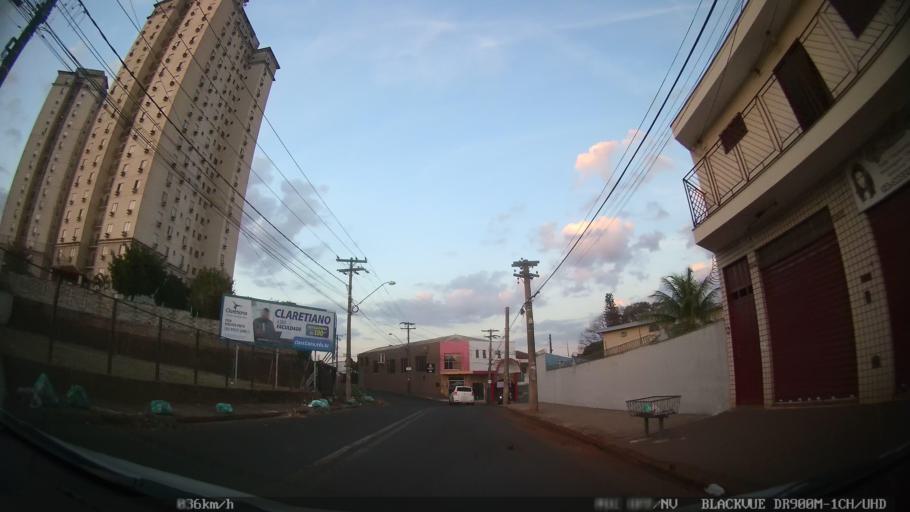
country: BR
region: Sao Paulo
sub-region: Ribeirao Preto
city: Ribeirao Preto
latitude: -21.1565
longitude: -47.8293
